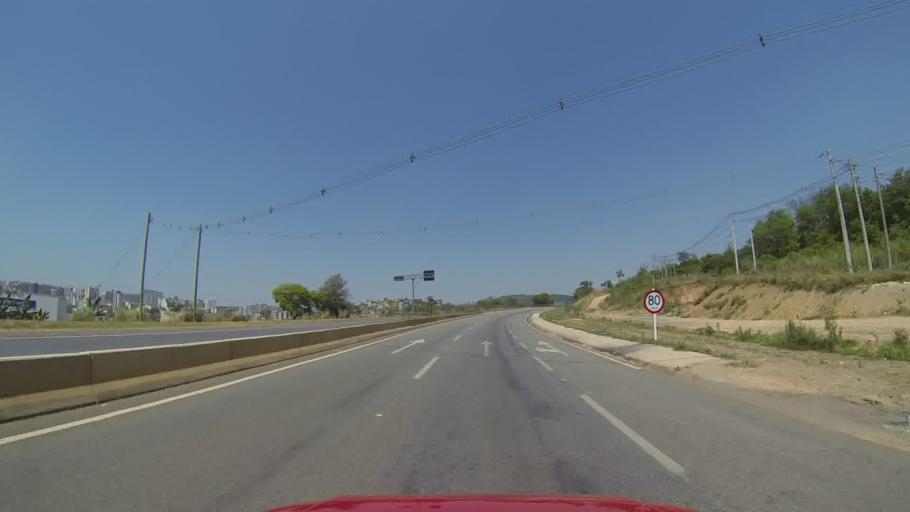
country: BR
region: Minas Gerais
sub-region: Itauna
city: Itauna
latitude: -20.0634
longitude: -44.5753
